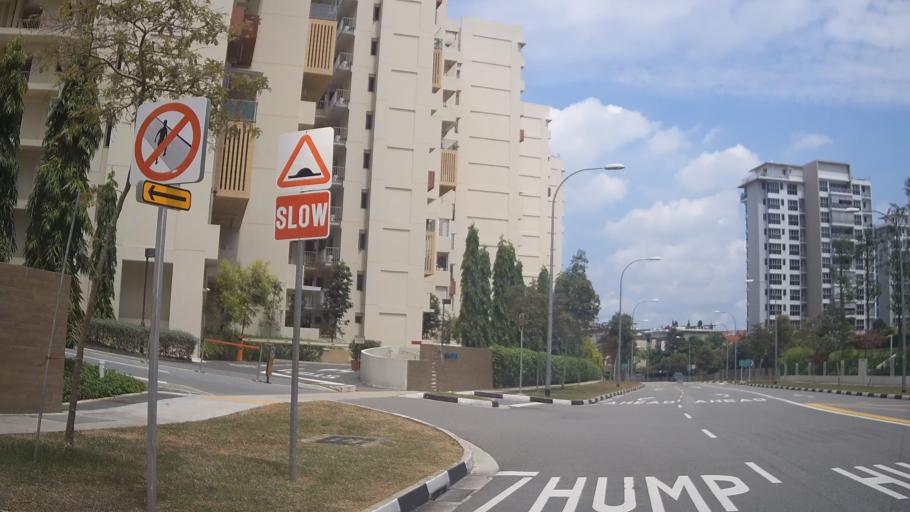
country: MY
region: Johor
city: Kampung Pasir Gudang Baru
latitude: 1.3760
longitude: 103.9590
